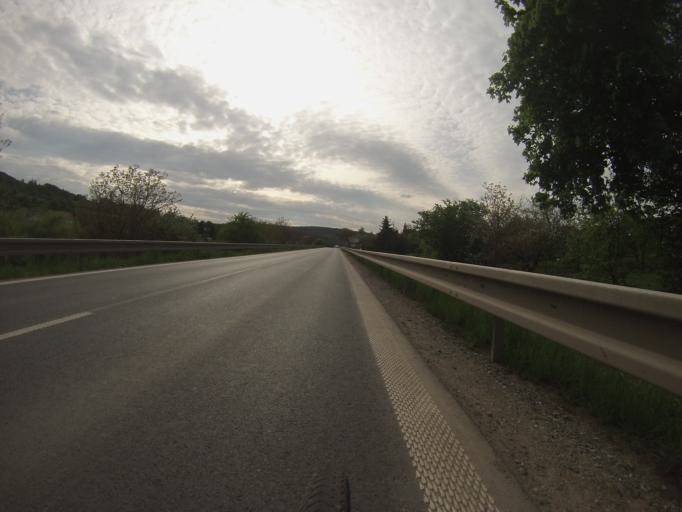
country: CZ
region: South Moravian
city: Drasov
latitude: 49.3258
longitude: 16.4476
